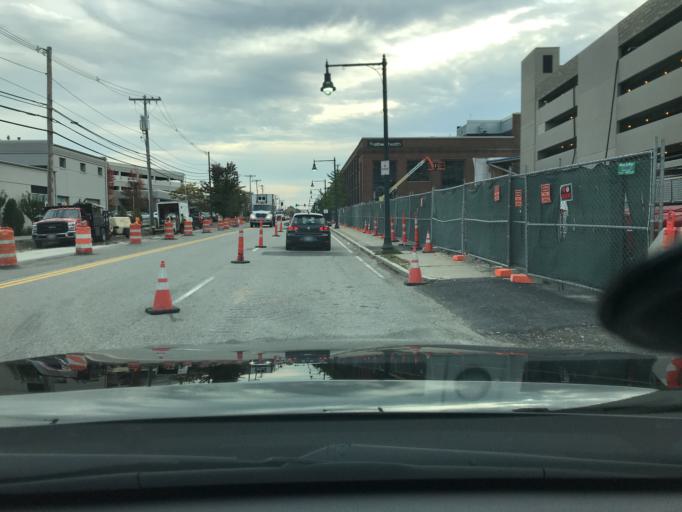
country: US
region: Massachusetts
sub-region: Middlesex County
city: Watertown
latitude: 42.3640
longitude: -71.1699
